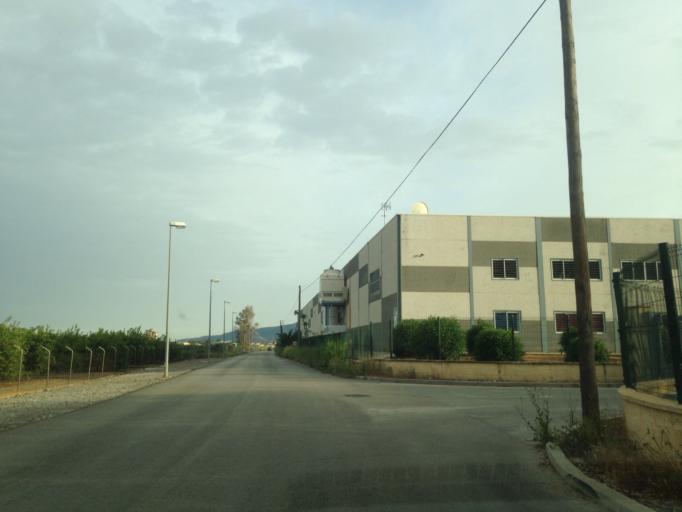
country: ES
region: Andalusia
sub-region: Provincia de Malaga
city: Alhaurin de la Torre
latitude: 36.7343
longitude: -4.5428
